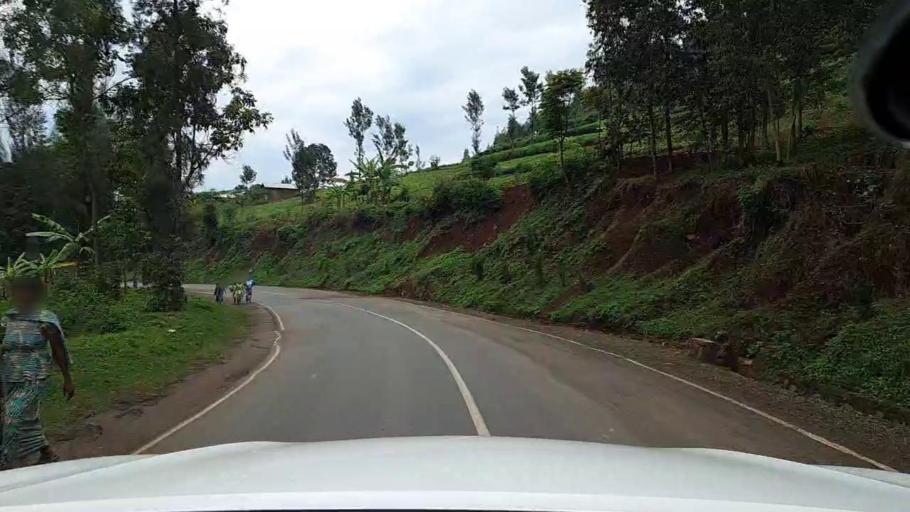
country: RW
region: Western Province
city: Cyangugu
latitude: -2.6511
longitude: 28.9670
